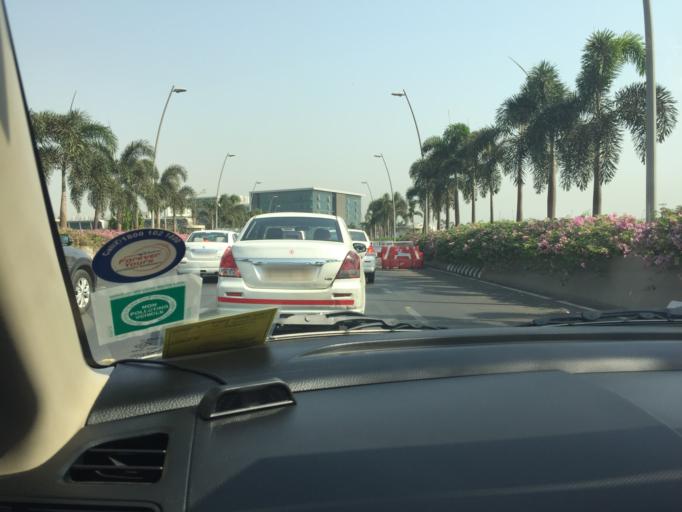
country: IN
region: Maharashtra
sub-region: Mumbai Suburban
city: Mumbai
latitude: 19.1008
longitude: 72.8738
